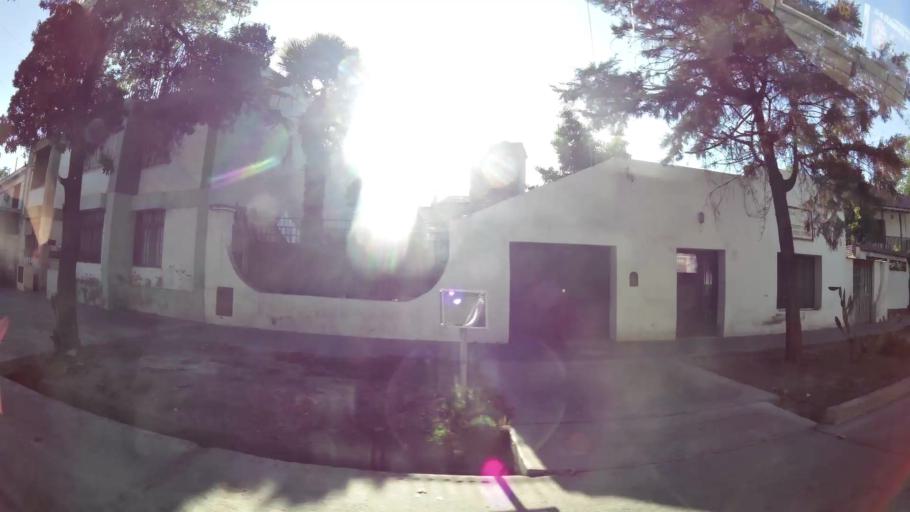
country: AR
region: Mendoza
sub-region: Departamento de Godoy Cruz
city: Godoy Cruz
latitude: -32.9179
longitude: -68.8507
